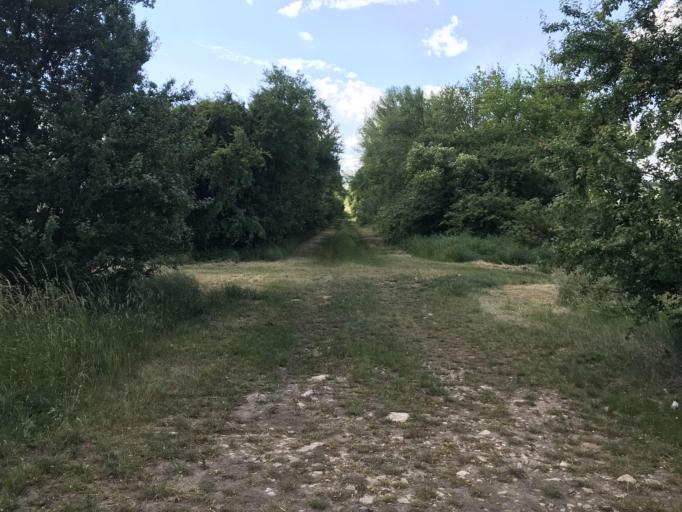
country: DE
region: Saxony-Anhalt
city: Schwanebeck
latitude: 51.9875
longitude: 11.1064
